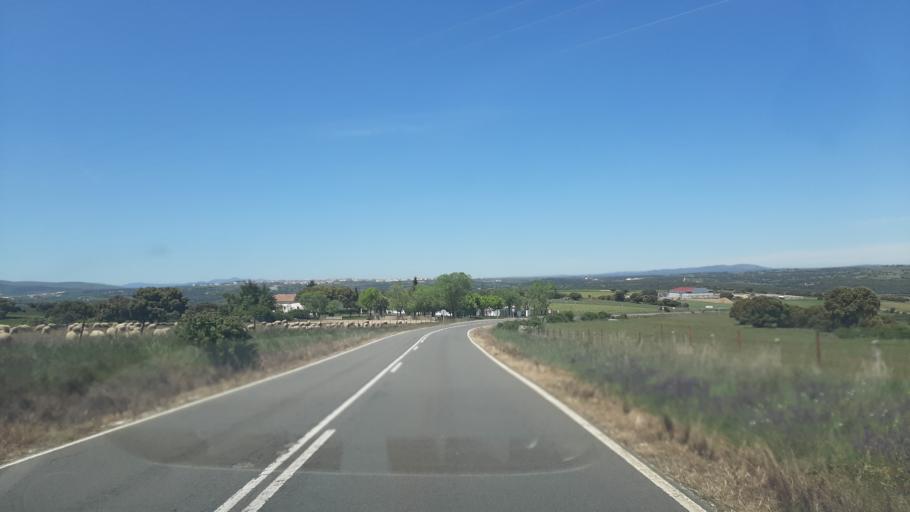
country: ES
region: Castille and Leon
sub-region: Provincia de Salamanca
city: Aldeavieja de Tormes
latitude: 40.5442
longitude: -5.5925
